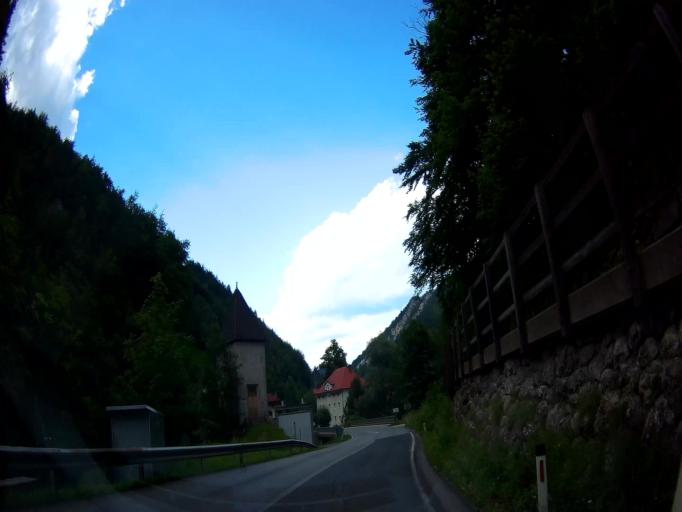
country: AT
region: Carinthia
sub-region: Politischer Bezirk Volkermarkt
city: Bad Eisenkappel
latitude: 46.4976
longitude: 14.5828
